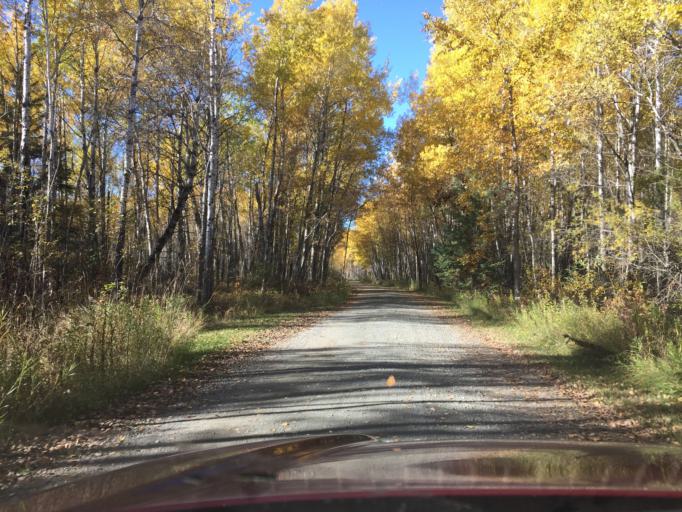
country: US
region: Minnesota
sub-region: Lake of the Woods County
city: Baudette
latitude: 48.2863
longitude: -94.5570
